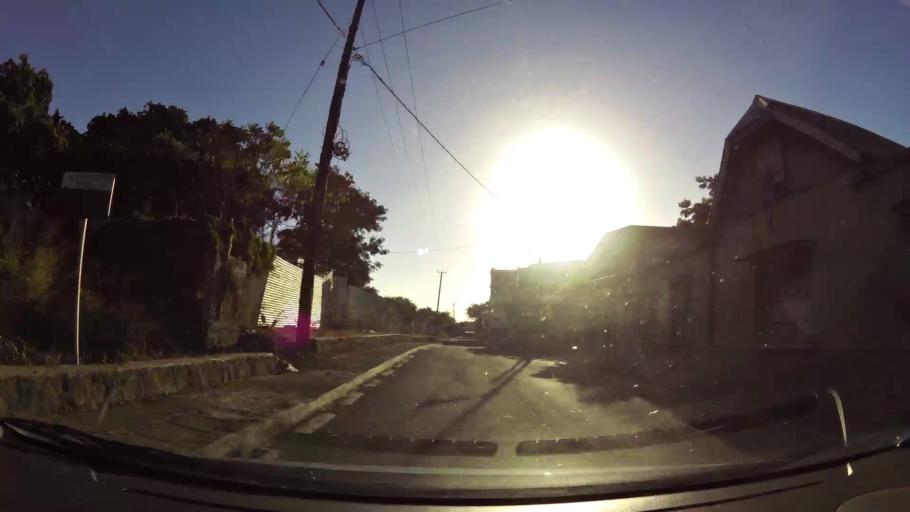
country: MU
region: Port Louis
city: Port Louis
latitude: -20.1672
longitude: 57.4929
